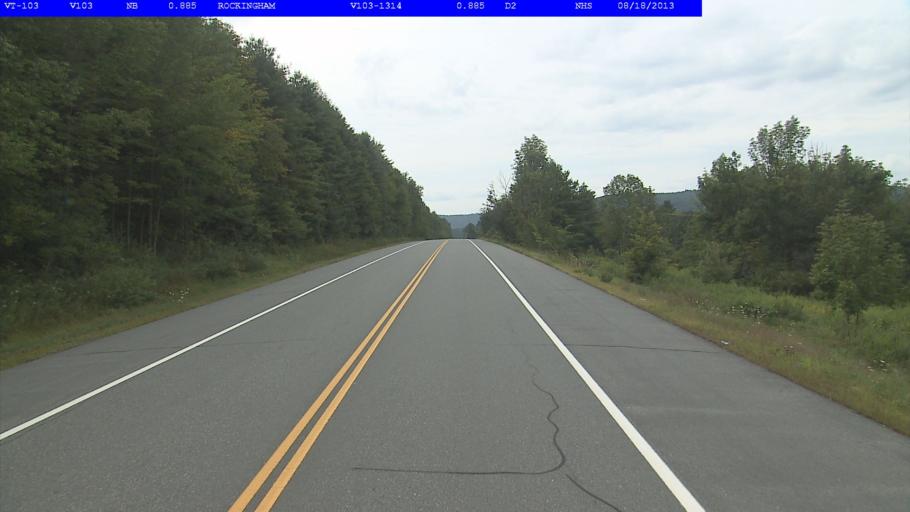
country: US
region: Vermont
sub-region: Windham County
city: Rockingham
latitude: 43.1829
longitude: -72.4751
